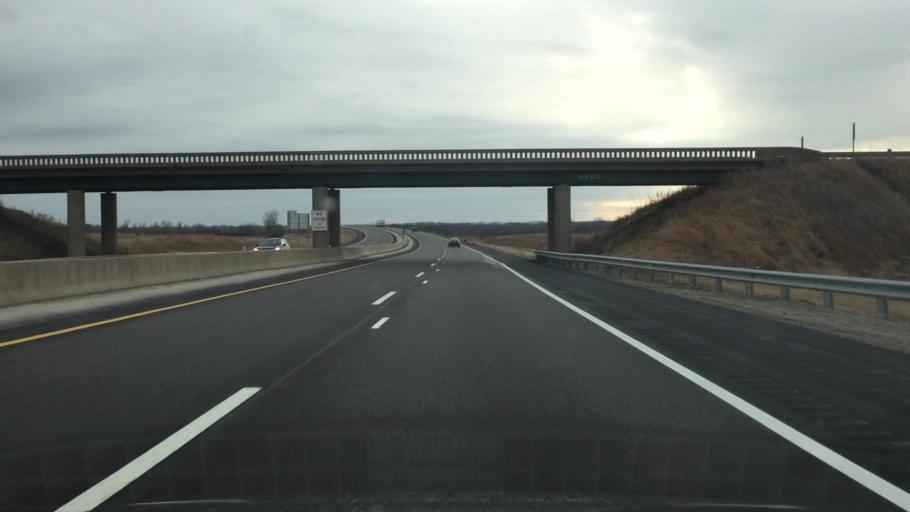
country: US
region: Kansas
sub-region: Osage County
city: Osage City
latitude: 38.6356
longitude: -96.0410
